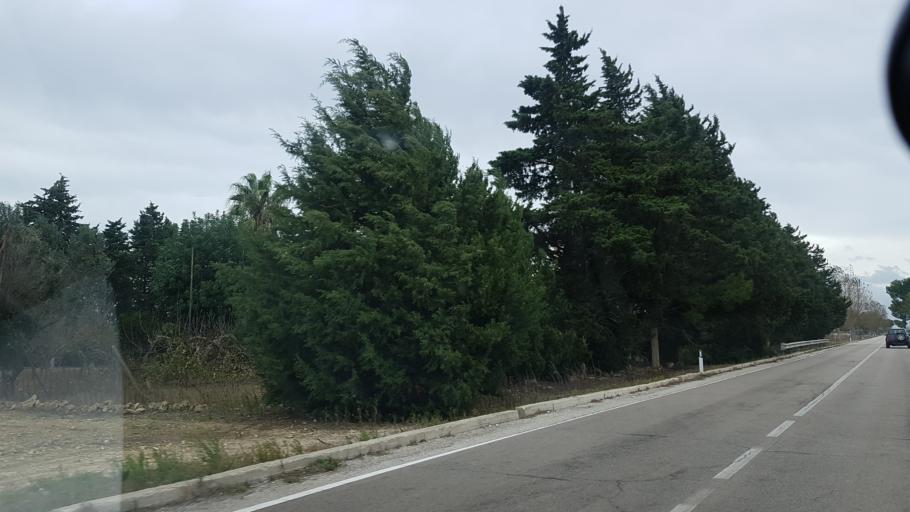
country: IT
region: Apulia
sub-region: Provincia di Brindisi
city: San Pancrazio Salentino
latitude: 40.4134
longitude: 17.8591
